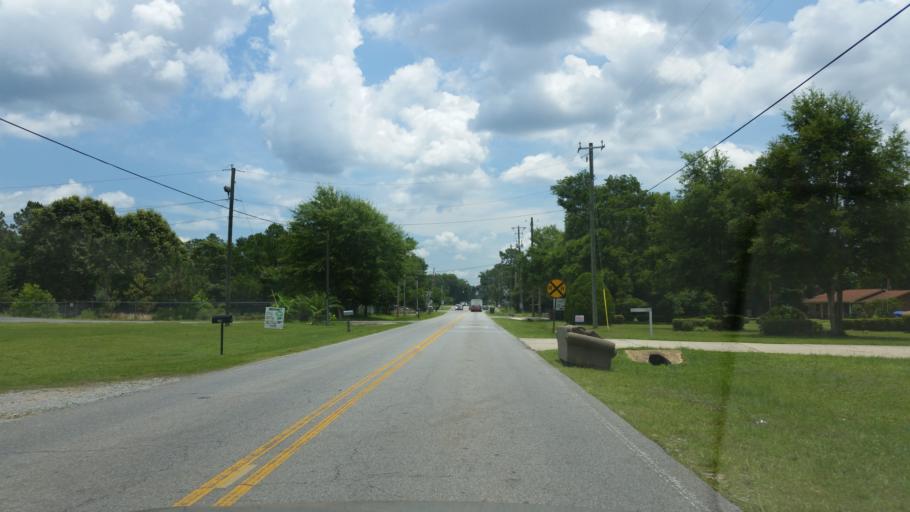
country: US
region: Florida
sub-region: Escambia County
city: Ensley
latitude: 30.5480
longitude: -87.2850
